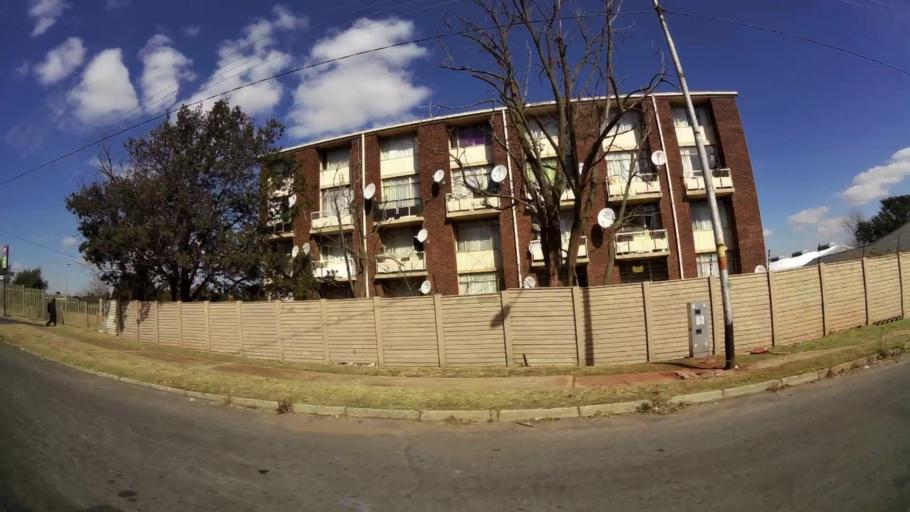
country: ZA
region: Gauteng
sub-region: West Rand District Municipality
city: Krugersdorp
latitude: -26.0994
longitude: 27.7812
